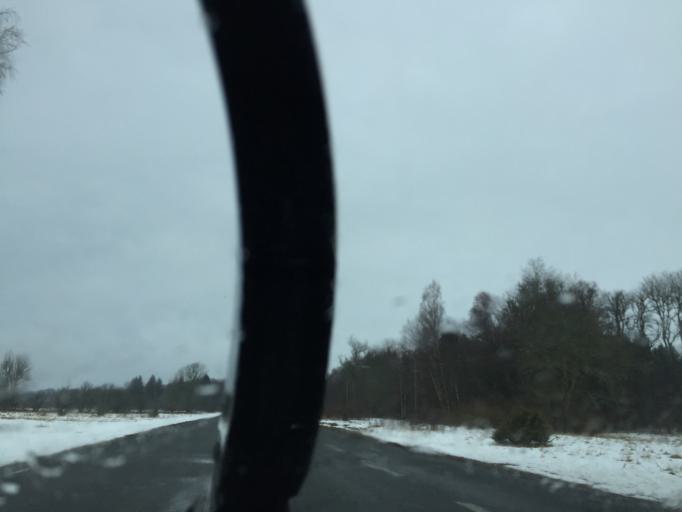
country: EE
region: Saare
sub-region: Kuressaare linn
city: Kuressaare
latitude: 58.3190
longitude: 22.0230
